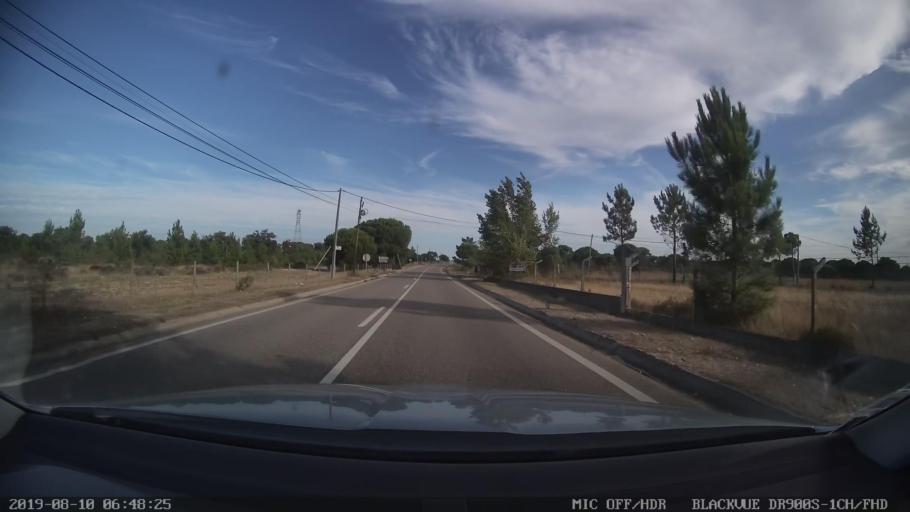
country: PT
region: Santarem
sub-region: Benavente
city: Benavente
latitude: 38.9304
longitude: -8.7788
